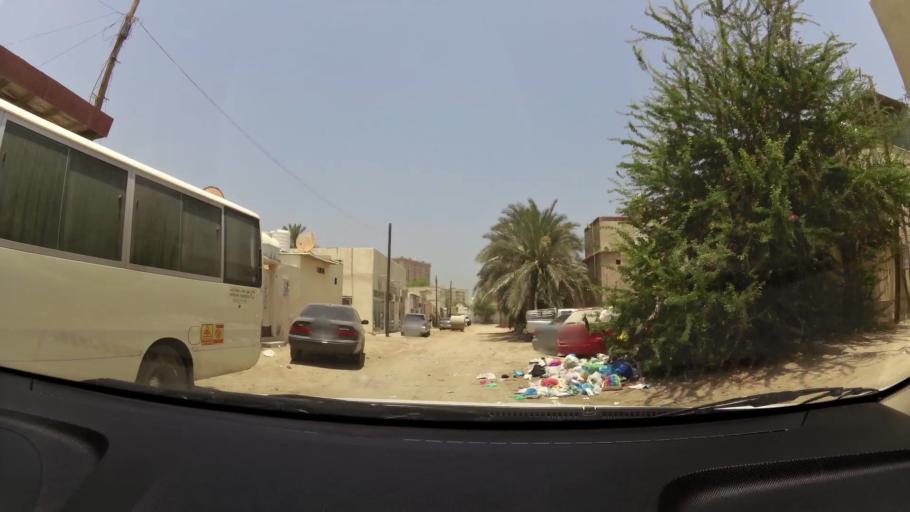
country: AE
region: Ajman
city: Ajman
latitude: 25.3969
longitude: 55.4376
